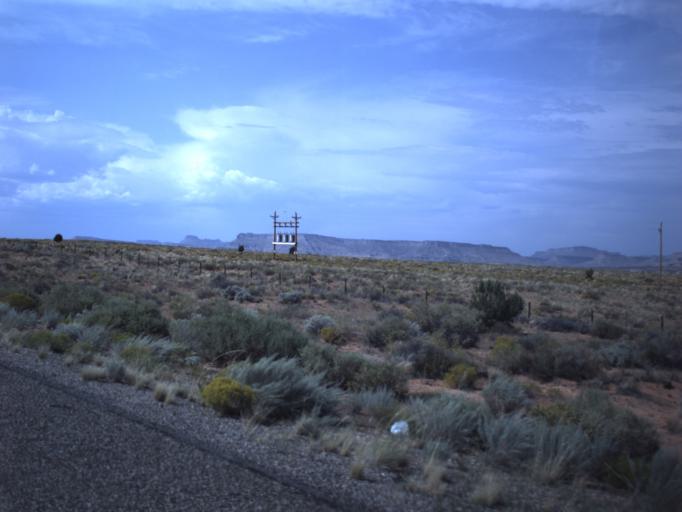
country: US
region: Arizona
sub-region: Coconino County
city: Page
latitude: 37.0845
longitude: -111.6798
